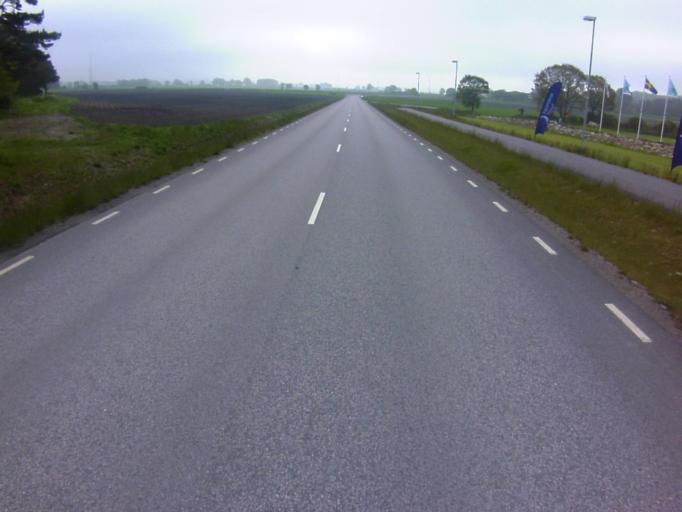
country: SE
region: Blekinge
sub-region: Solvesborgs Kommun
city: Soelvesborg
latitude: 56.0440
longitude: 14.6143
